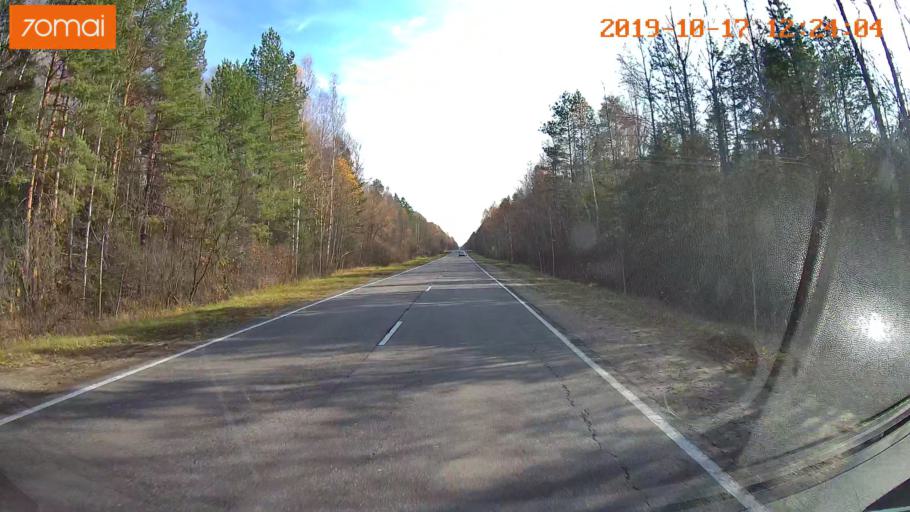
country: RU
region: Rjazan
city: Gus'-Zheleznyy
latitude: 55.0386
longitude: 41.2072
